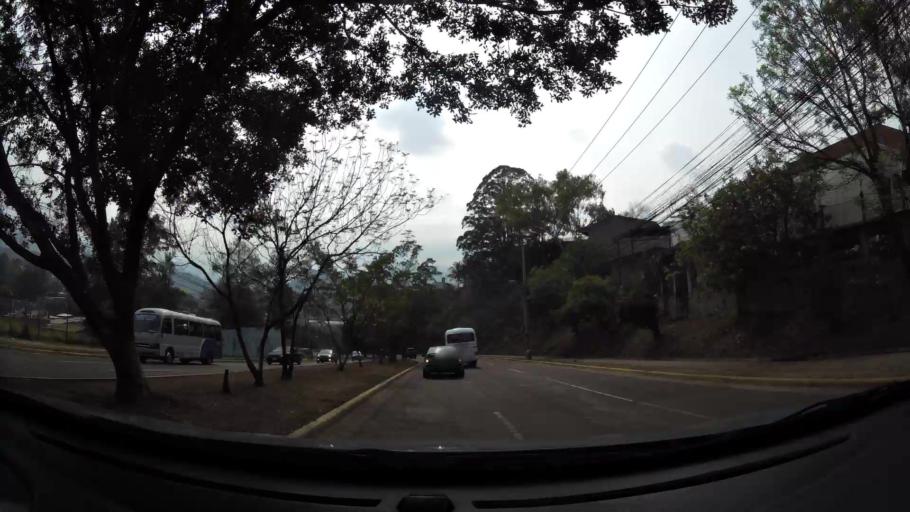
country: HN
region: Francisco Morazan
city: Tegucigalpa
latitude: 14.1031
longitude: -87.1764
